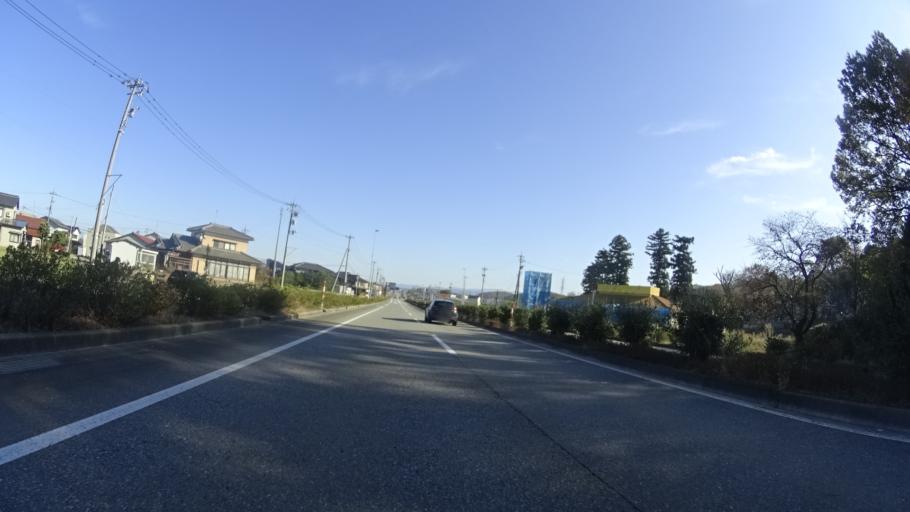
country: JP
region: Ishikawa
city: Komatsu
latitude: 36.3203
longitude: 136.4000
